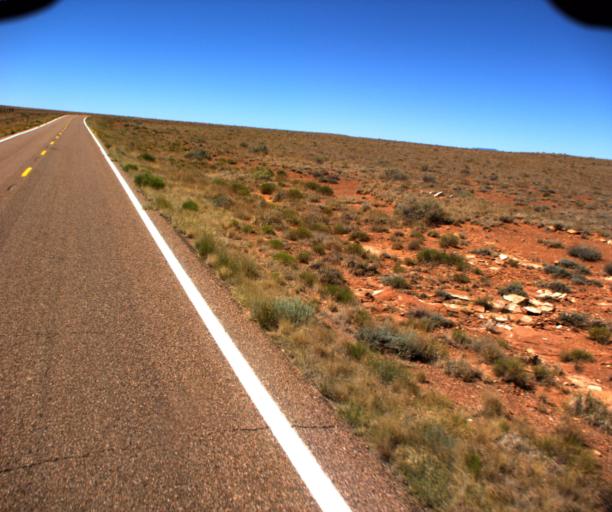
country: US
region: Arizona
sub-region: Navajo County
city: Winslow
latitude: 34.9189
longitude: -110.6378
